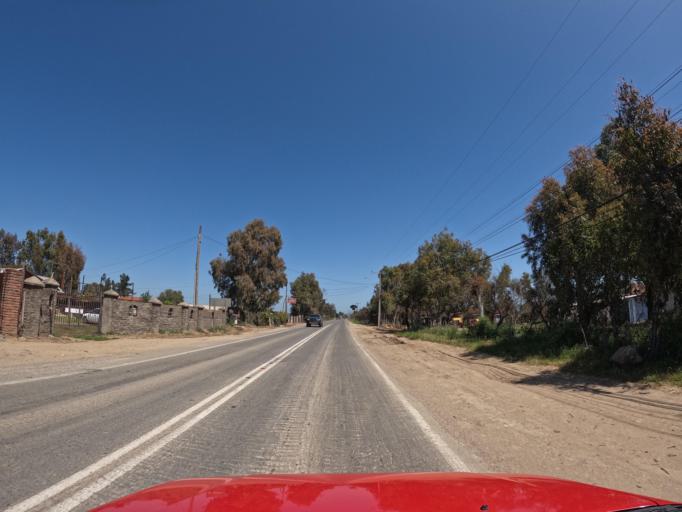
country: CL
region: O'Higgins
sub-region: Provincia de Colchagua
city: Santa Cruz
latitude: -34.7332
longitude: -71.6858
